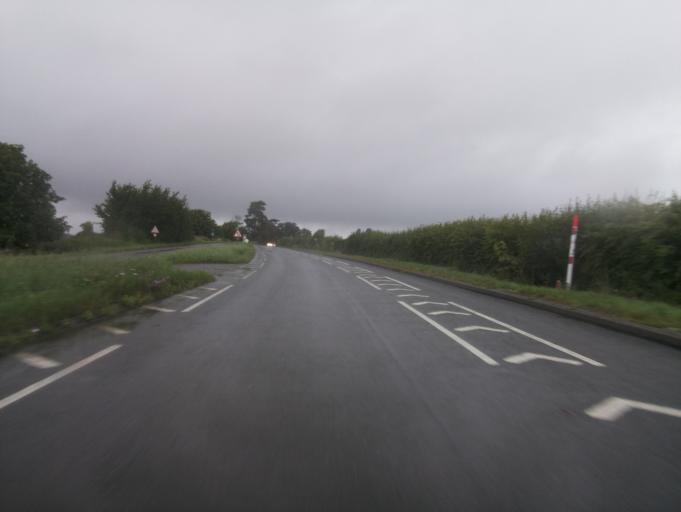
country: GB
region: England
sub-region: Gloucestershire
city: Tewkesbury
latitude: 51.9719
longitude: -2.1562
